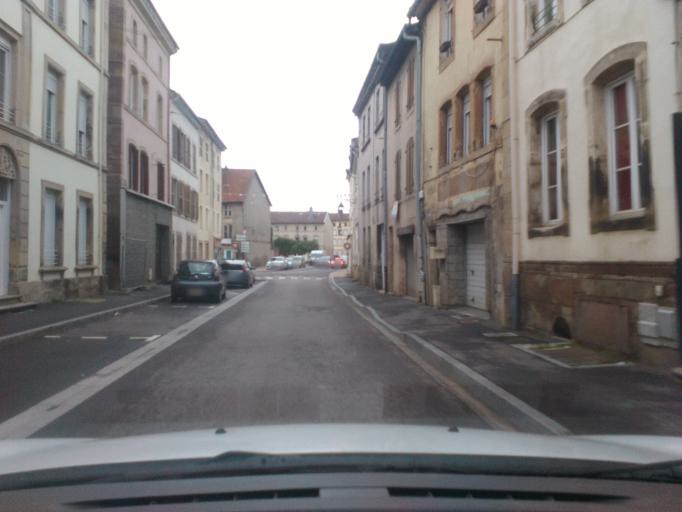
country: FR
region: Lorraine
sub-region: Departement des Vosges
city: Rambervillers
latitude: 48.3468
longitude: 6.6364
